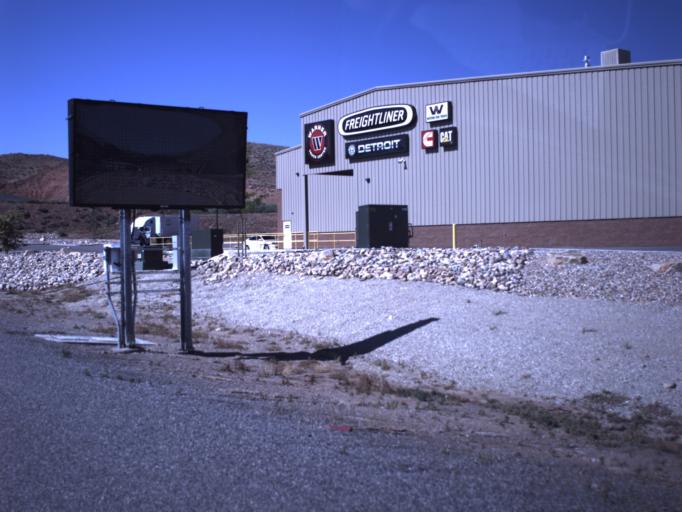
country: US
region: Utah
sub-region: Sevier County
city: Salina
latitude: 38.9402
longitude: -111.8546
